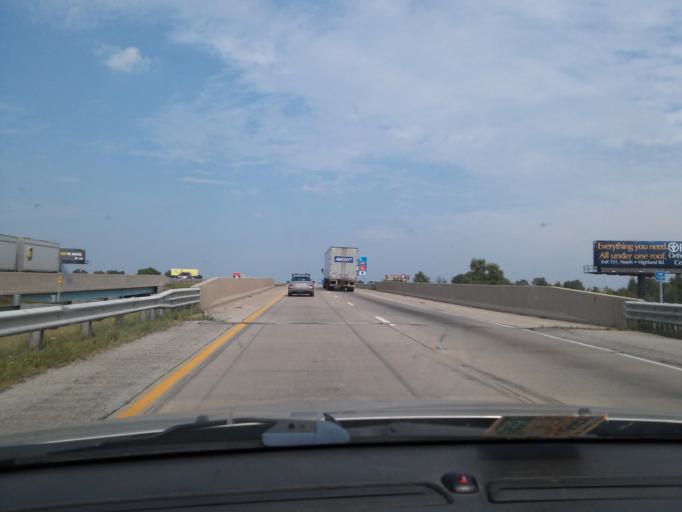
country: US
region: Indiana
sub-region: Wayne County
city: Richmond
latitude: 39.8692
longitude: -84.9129
